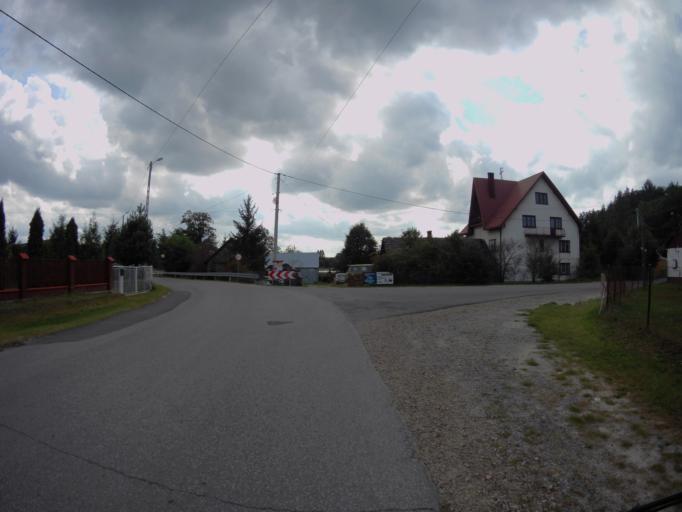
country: PL
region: Subcarpathian Voivodeship
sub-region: Powiat lezajski
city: Brzoza Krolewska
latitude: 50.2403
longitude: 22.3223
